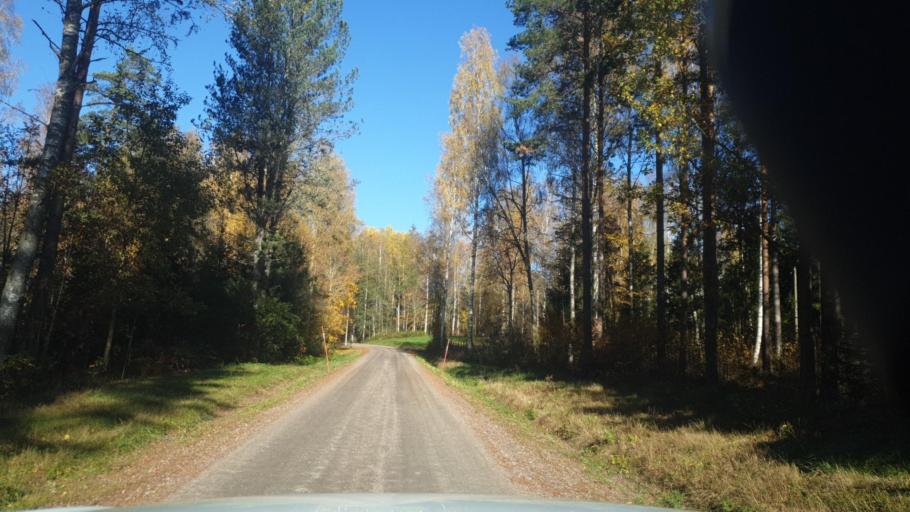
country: SE
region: Vaermland
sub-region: Arvika Kommun
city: Arvika
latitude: 59.5070
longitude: 12.7317
